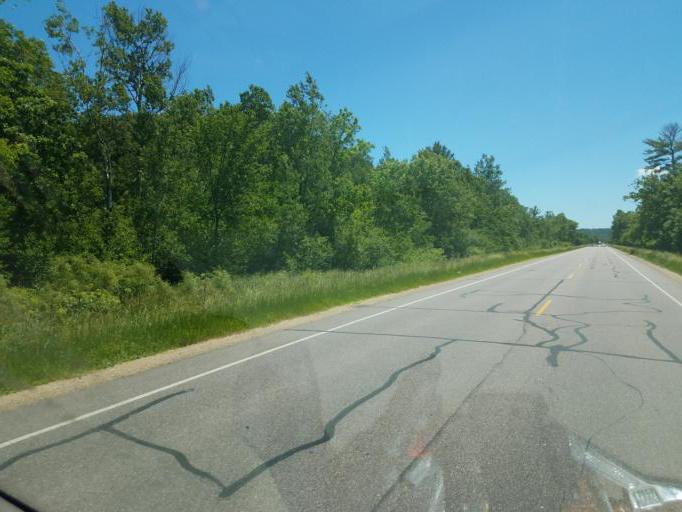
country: US
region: Wisconsin
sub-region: Juneau County
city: Elroy
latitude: 43.6967
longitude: -90.2665
